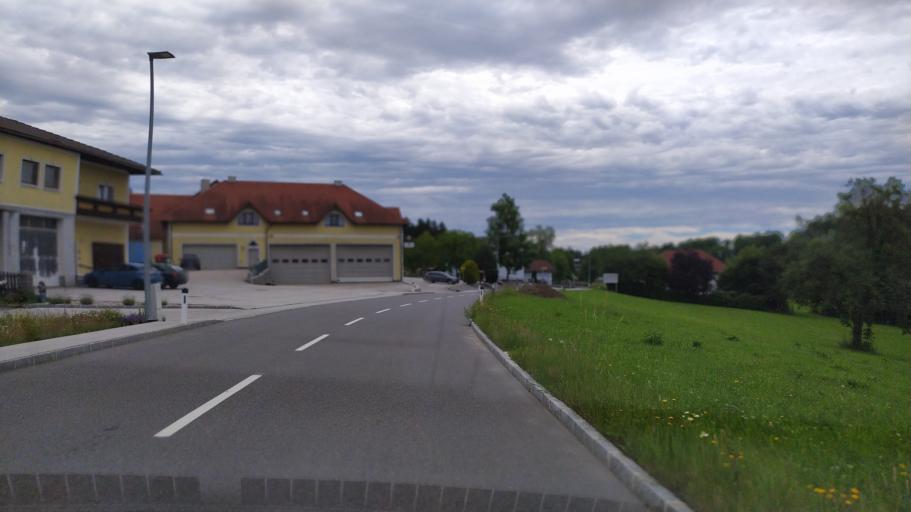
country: AT
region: Upper Austria
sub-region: Politischer Bezirk Perg
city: Perg
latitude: 48.2604
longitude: 14.6543
